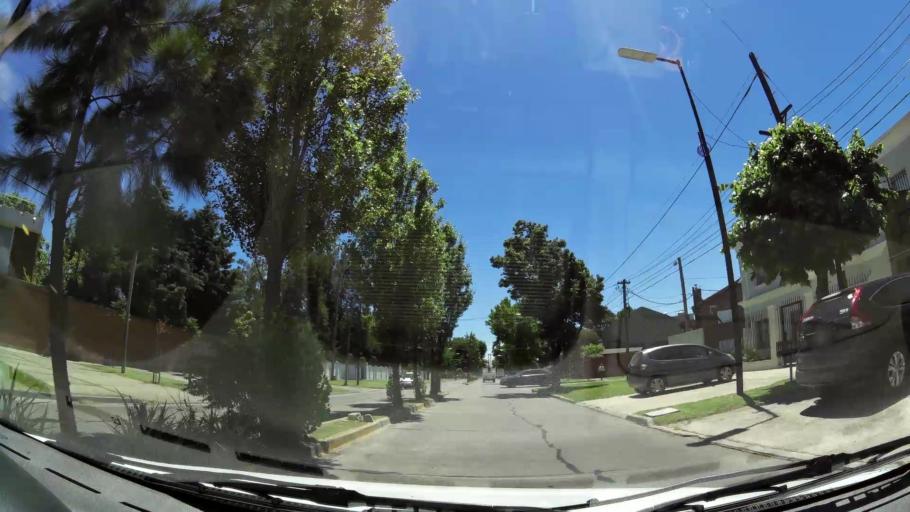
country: AR
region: Buenos Aires
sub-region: Partido de San Isidro
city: San Isidro
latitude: -34.4989
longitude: -58.5598
